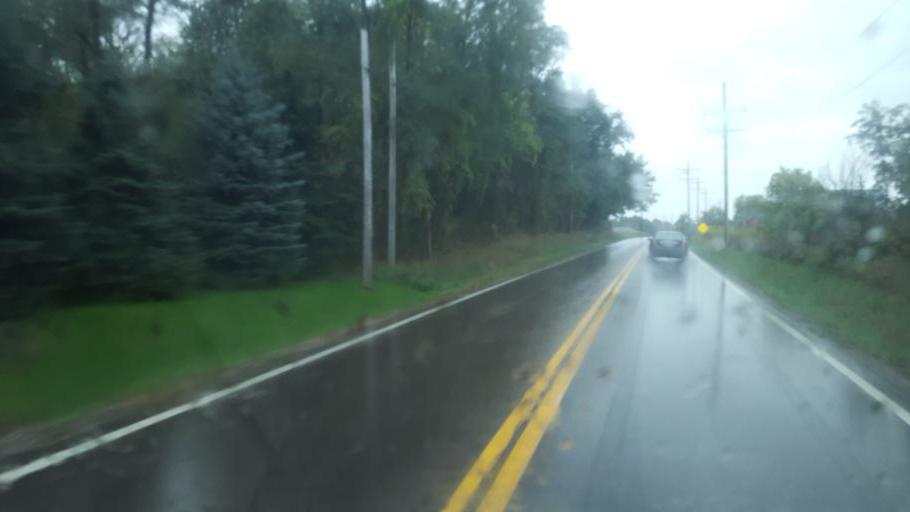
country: US
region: Ohio
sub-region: Richland County
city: Lincoln Heights
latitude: 40.8214
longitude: -82.4837
